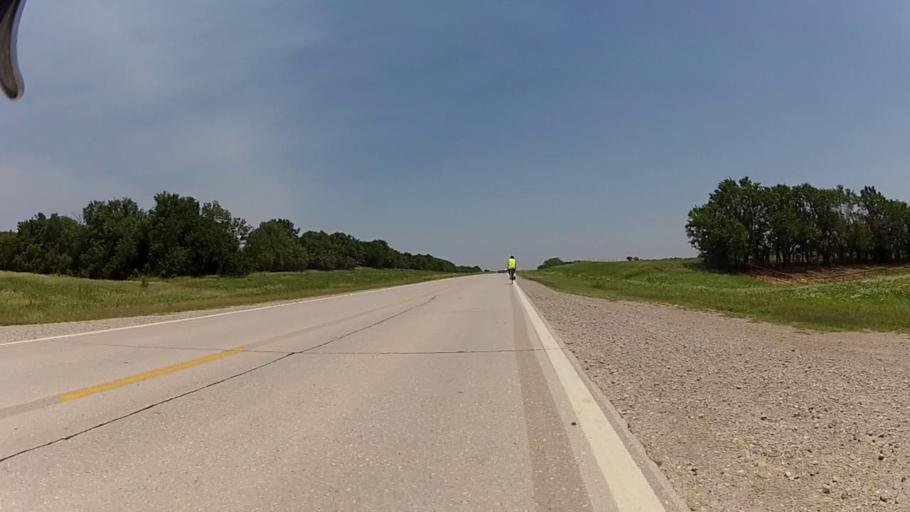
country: US
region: Kansas
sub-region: Sumner County
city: Wellington
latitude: 37.0567
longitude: -97.3929
